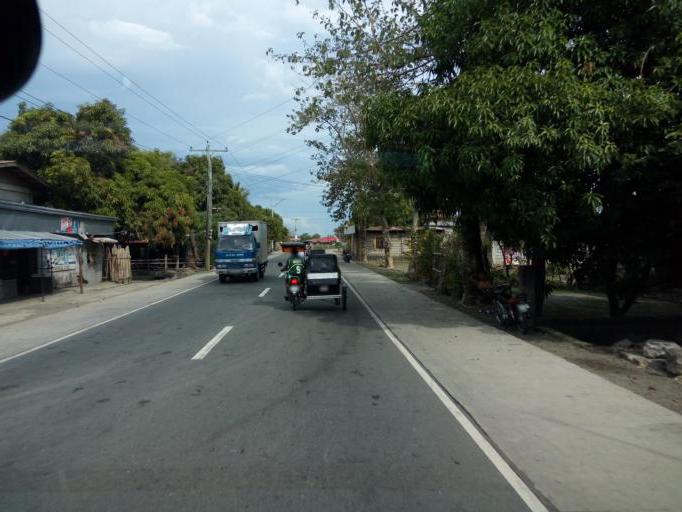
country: PH
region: Central Luzon
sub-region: Province of Nueva Ecija
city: Parista
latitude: 15.8210
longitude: 120.9552
